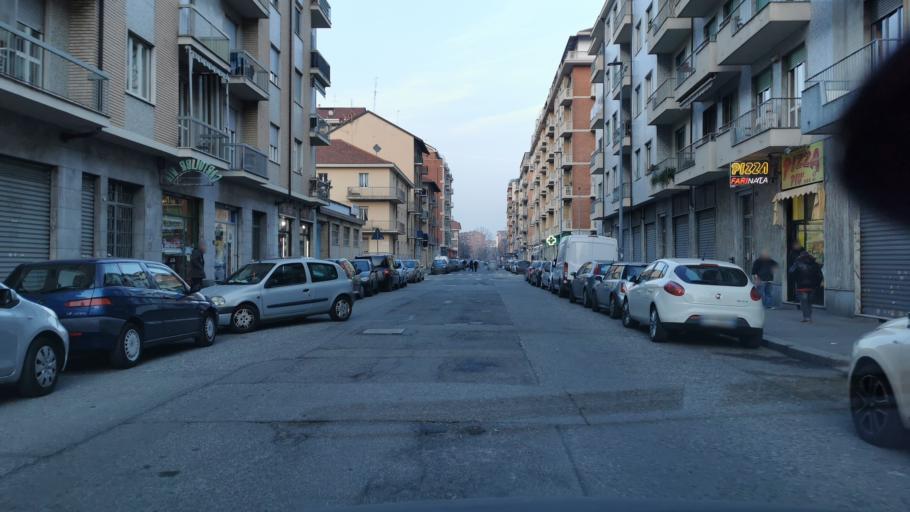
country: IT
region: Piedmont
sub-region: Provincia di Torino
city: Venaria Reale
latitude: 45.0988
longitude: 7.6539
